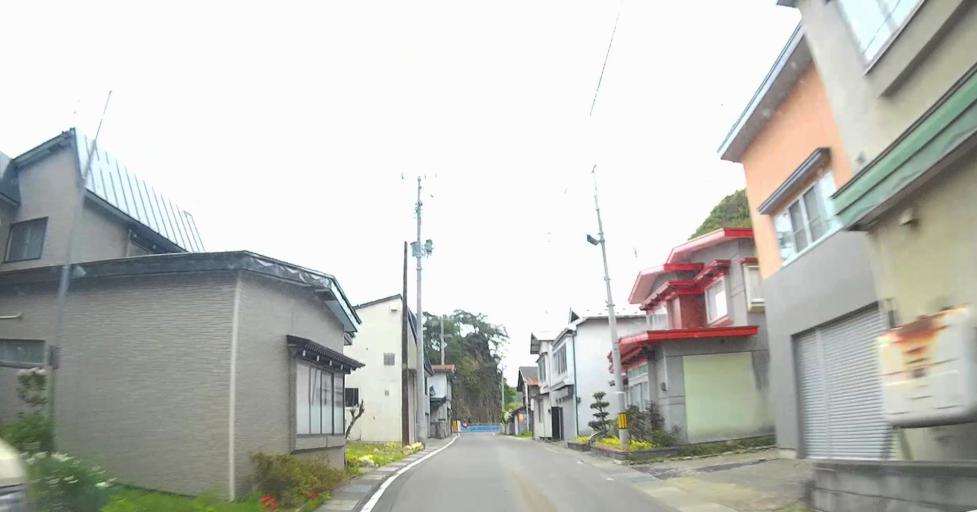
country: JP
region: Aomori
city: Shimokizukuri
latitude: 41.2000
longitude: 140.4299
